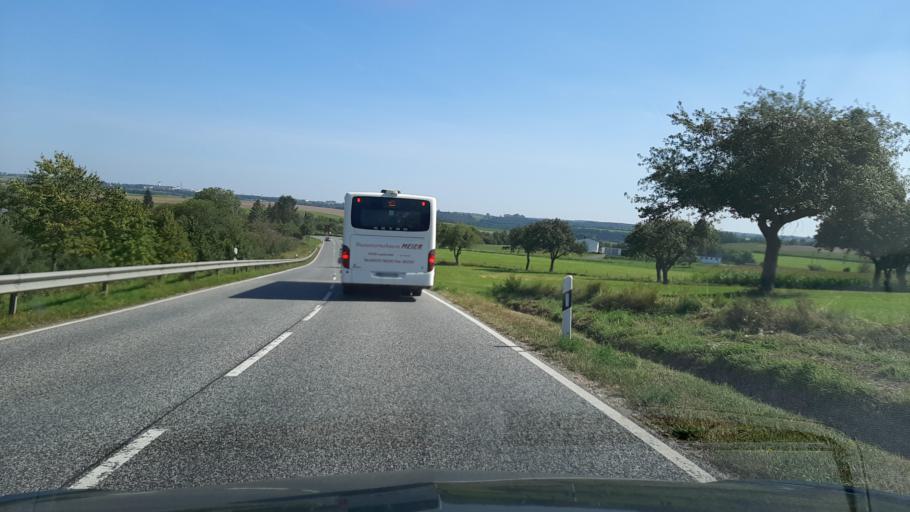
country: DE
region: Rheinland-Pfalz
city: Dudeldorf
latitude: 49.9707
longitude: 6.6307
